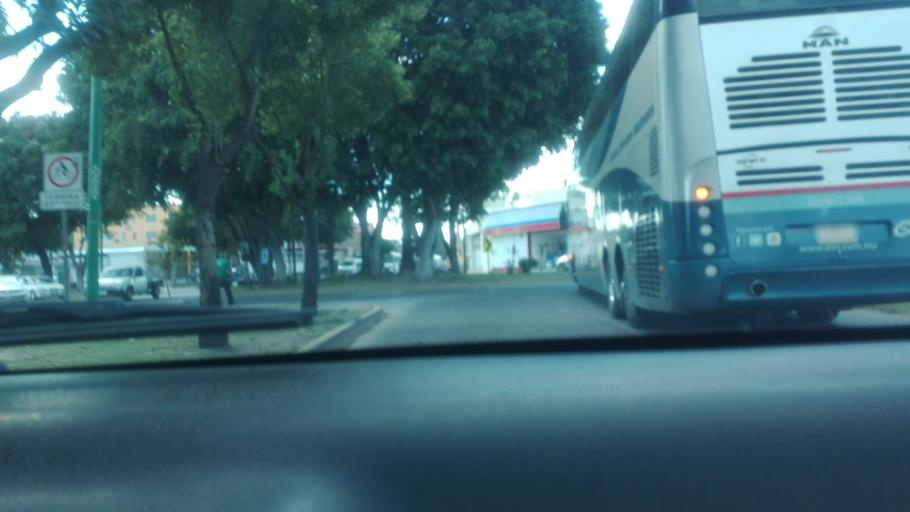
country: MX
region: Guanajuato
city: Leon
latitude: 21.1212
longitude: -101.6563
